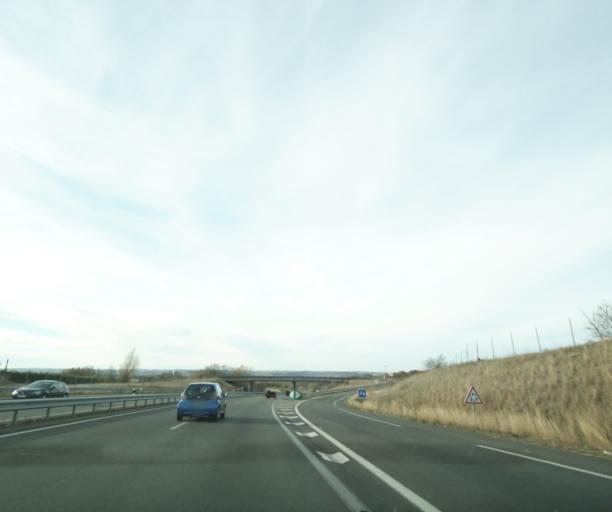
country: FR
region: Midi-Pyrenees
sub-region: Departement du Gers
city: Pujaudran
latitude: 43.5960
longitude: 1.1136
